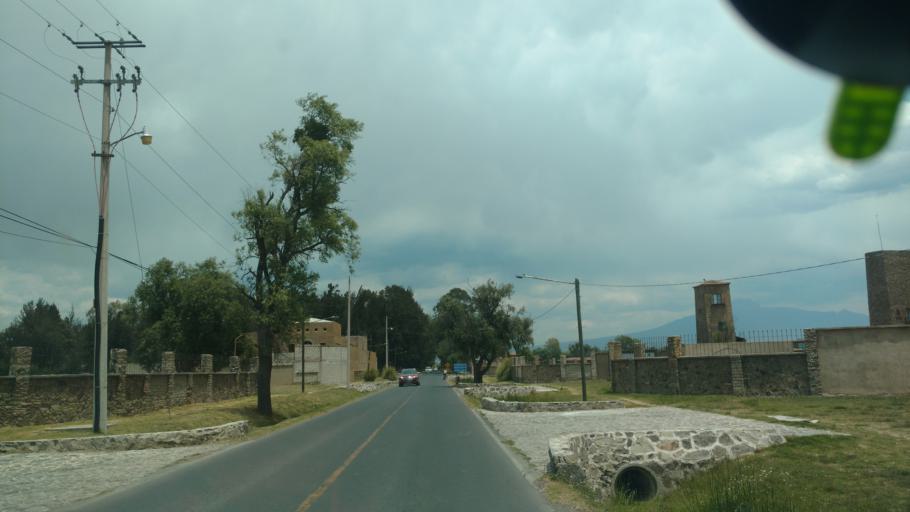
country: MX
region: Puebla
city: San Miguel Xoxtla
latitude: 19.1876
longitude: -98.2938
